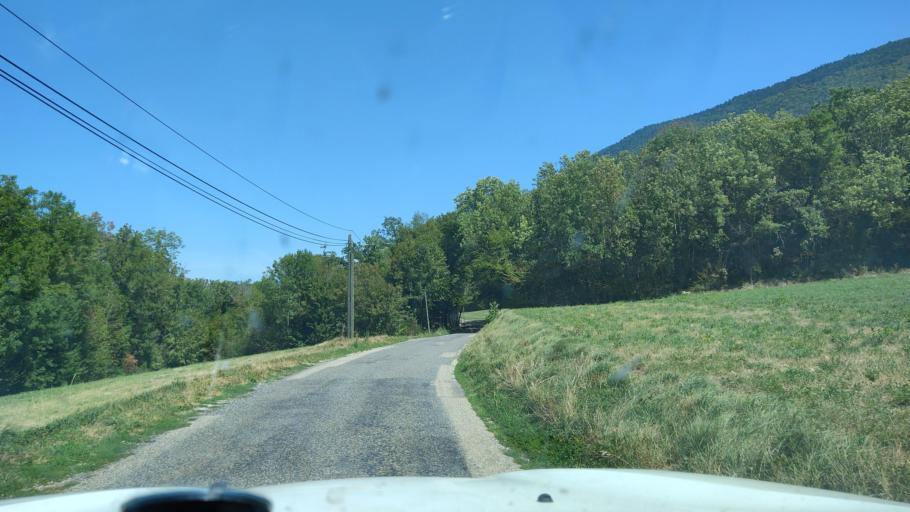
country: FR
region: Rhone-Alpes
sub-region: Departement de la Savoie
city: Novalaise
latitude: 45.6446
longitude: 5.7851
